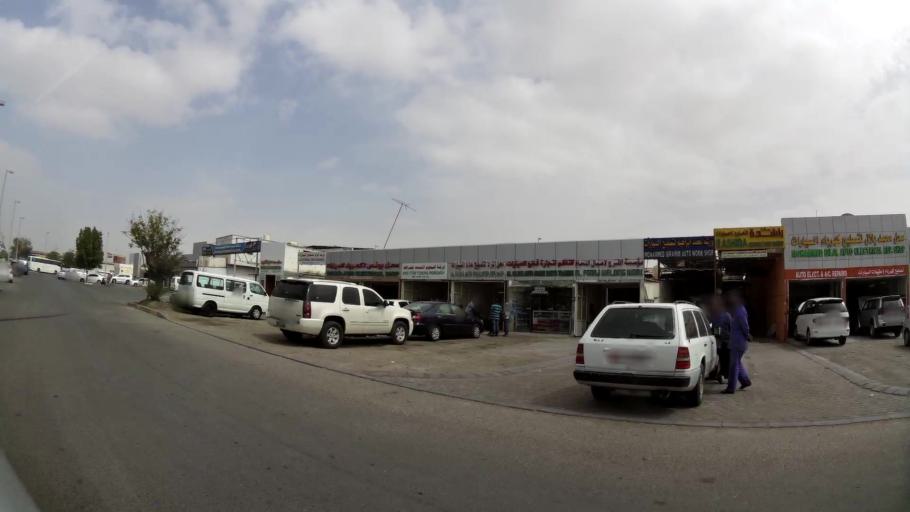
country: AE
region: Abu Dhabi
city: Abu Dhabi
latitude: 24.3810
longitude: 54.5147
